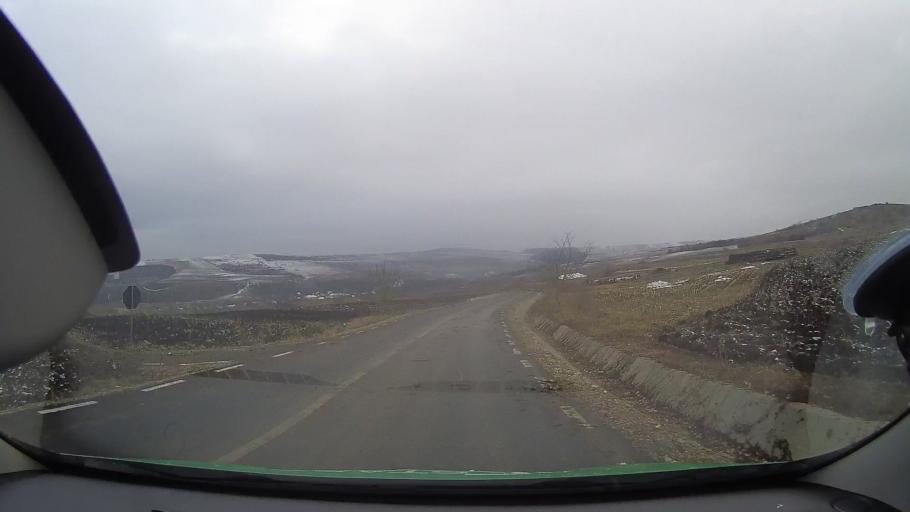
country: RO
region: Alba
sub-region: Comuna Farau
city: Farau
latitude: 46.3954
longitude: 24.0211
